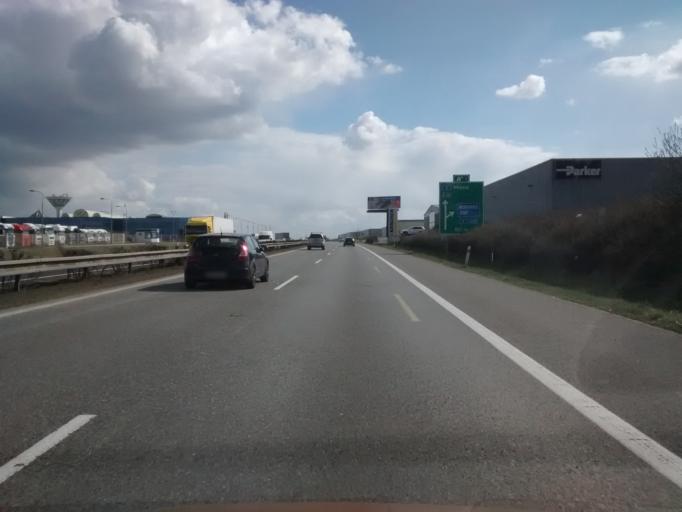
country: CZ
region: Central Bohemia
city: Zdiby
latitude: 50.1842
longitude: 14.4463
